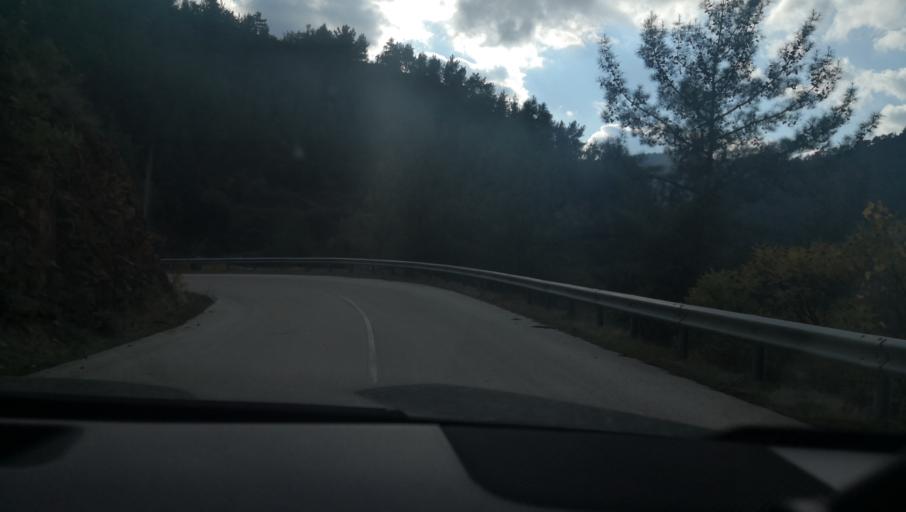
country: CY
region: Lefkosia
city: Lefka
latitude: 35.0499
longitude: 32.7410
